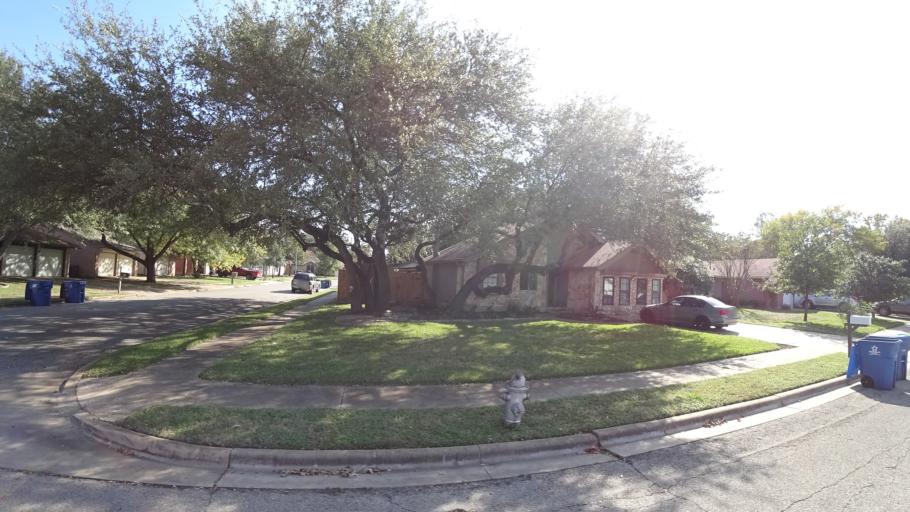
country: US
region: Texas
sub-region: Williamson County
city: Anderson Mill
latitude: 30.4514
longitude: -97.7997
